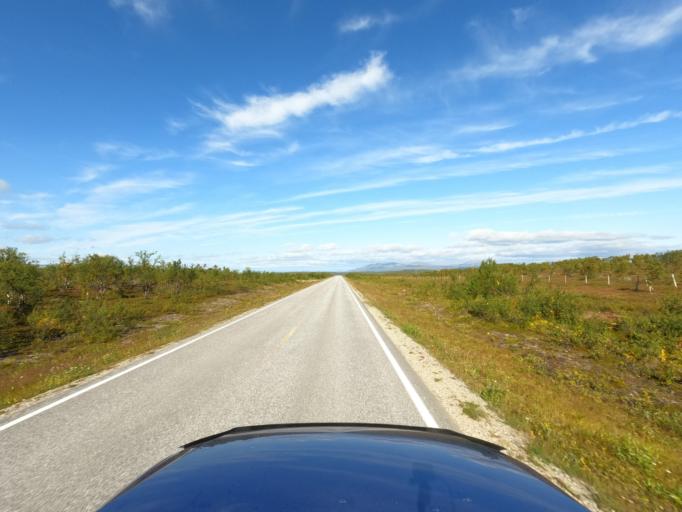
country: NO
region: Finnmark Fylke
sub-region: Karasjok
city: Karasjohka
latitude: 69.7179
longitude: 25.2402
